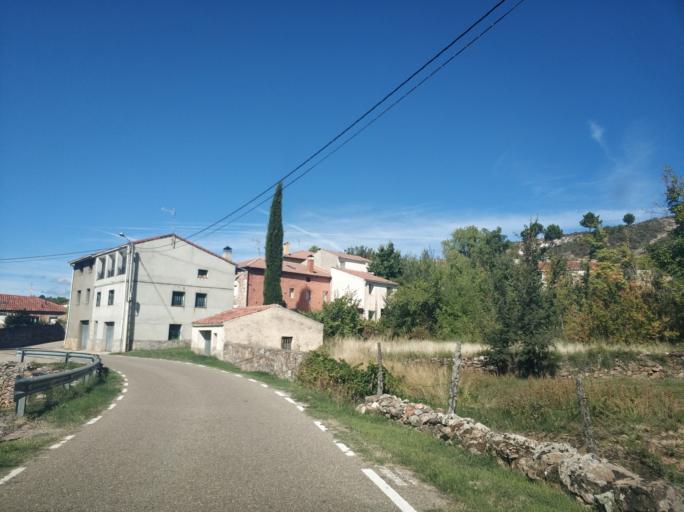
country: ES
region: Castille and Leon
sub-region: Provincia de Soria
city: Espeja de San Marcelino
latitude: 41.8020
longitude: -3.2201
